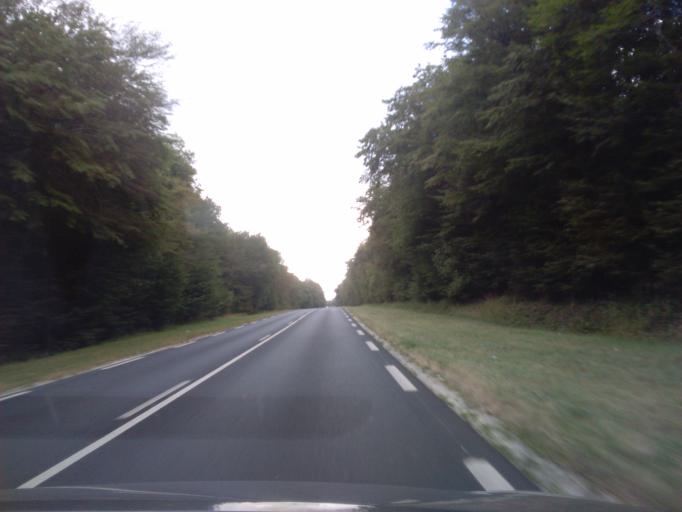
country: FR
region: Centre
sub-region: Departement du Loir-et-Cher
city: Cellettes
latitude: 47.5441
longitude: 1.3746
